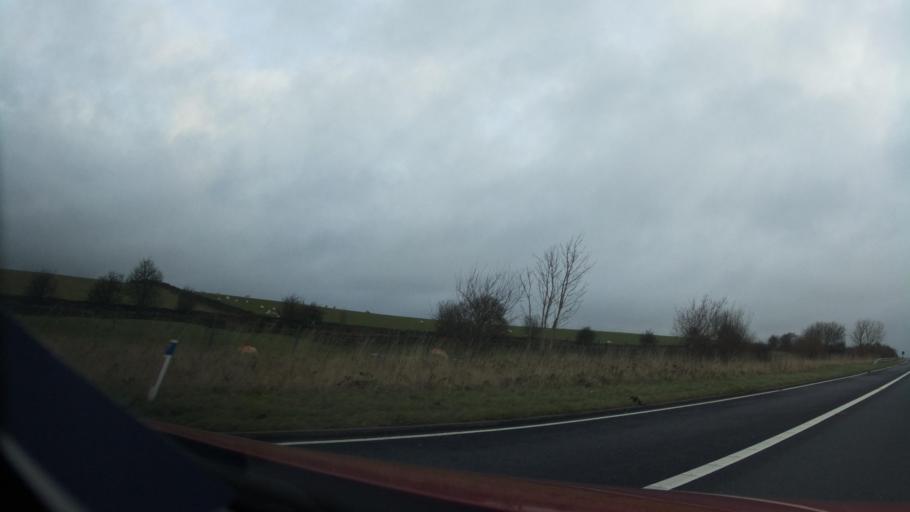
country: GB
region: England
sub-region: Cumbria
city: Kendal
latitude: 54.2754
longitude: -2.6733
